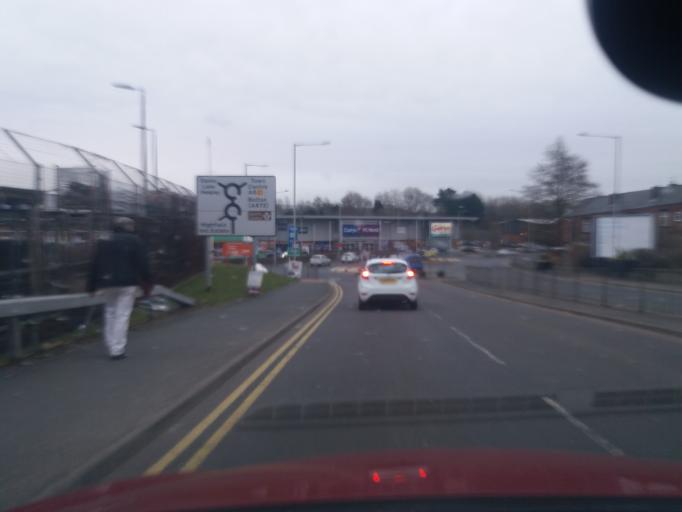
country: GB
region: England
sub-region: Lancashire
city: Chorley
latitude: 53.6613
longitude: -2.6294
